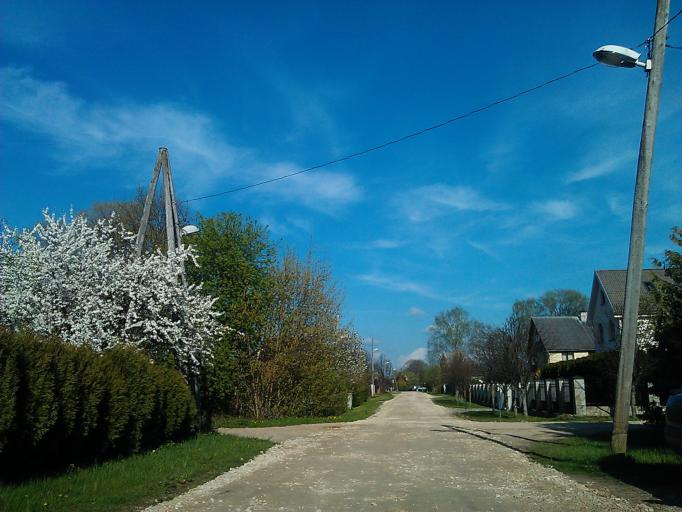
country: LV
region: Adazi
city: Adazi
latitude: 57.0719
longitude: 24.3287
